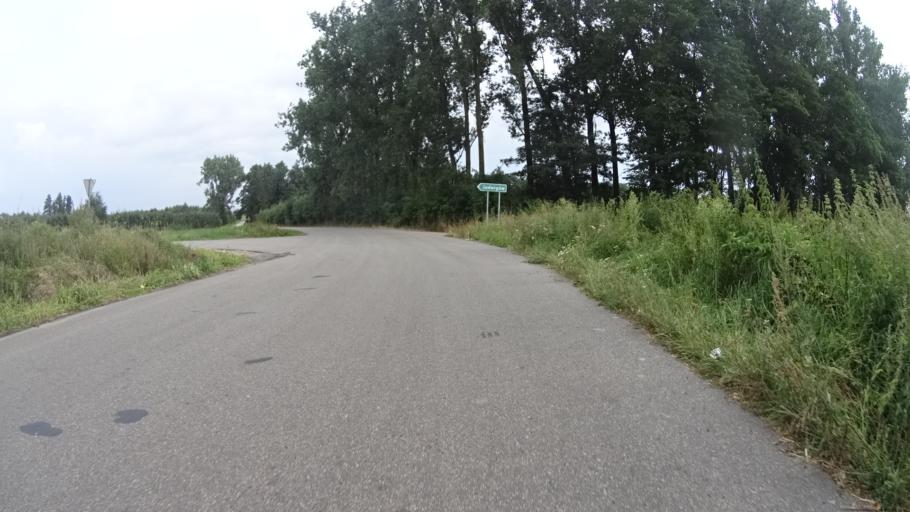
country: PL
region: Masovian Voivodeship
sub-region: Powiat grojecki
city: Goszczyn
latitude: 51.6894
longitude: 20.8579
